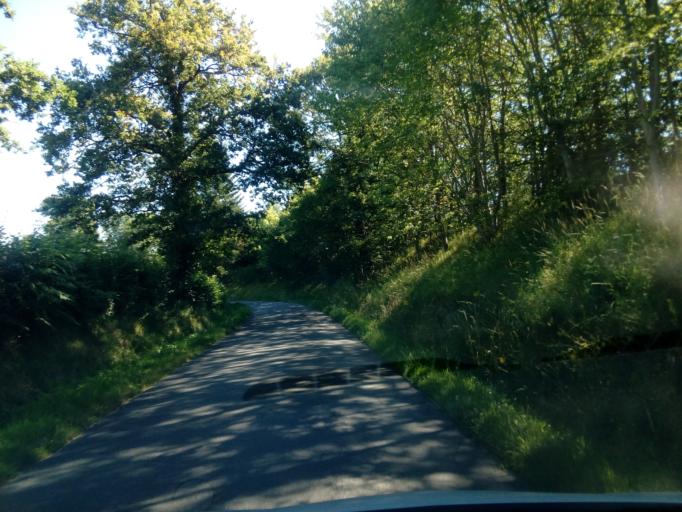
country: FR
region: Limousin
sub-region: Departement de la Creuse
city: Gueret
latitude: 46.1986
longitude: 1.8836
